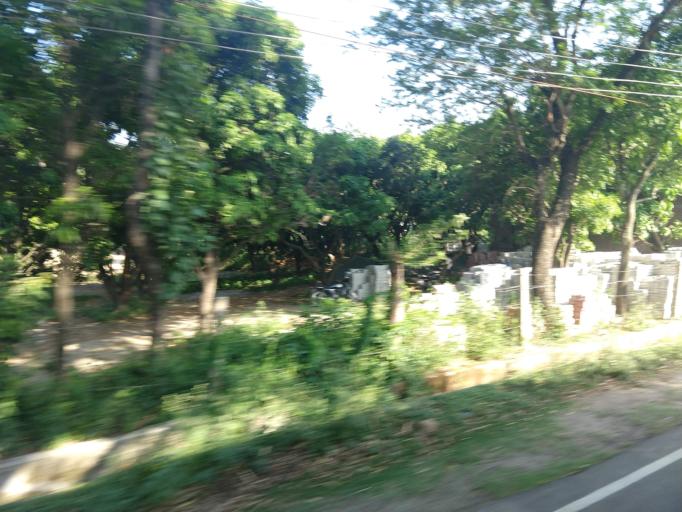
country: IN
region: Himachal Pradesh
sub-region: Chamba
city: Chowari
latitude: 32.3494
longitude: 75.9121
